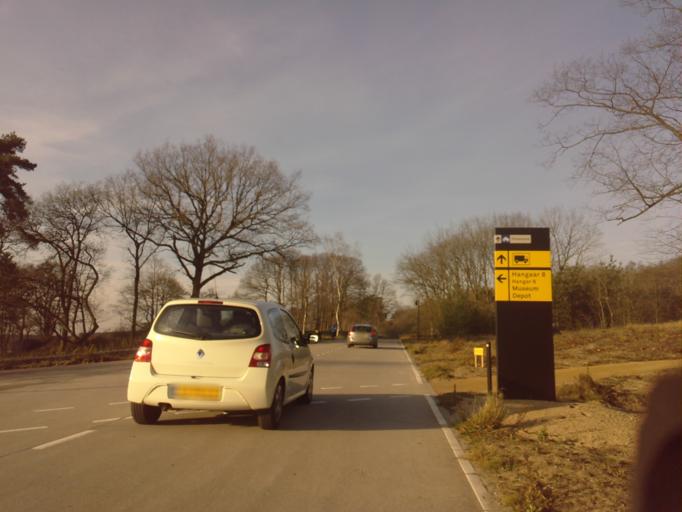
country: NL
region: Utrecht
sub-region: Gemeente Soest
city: Soest
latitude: 52.1345
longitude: 5.2744
